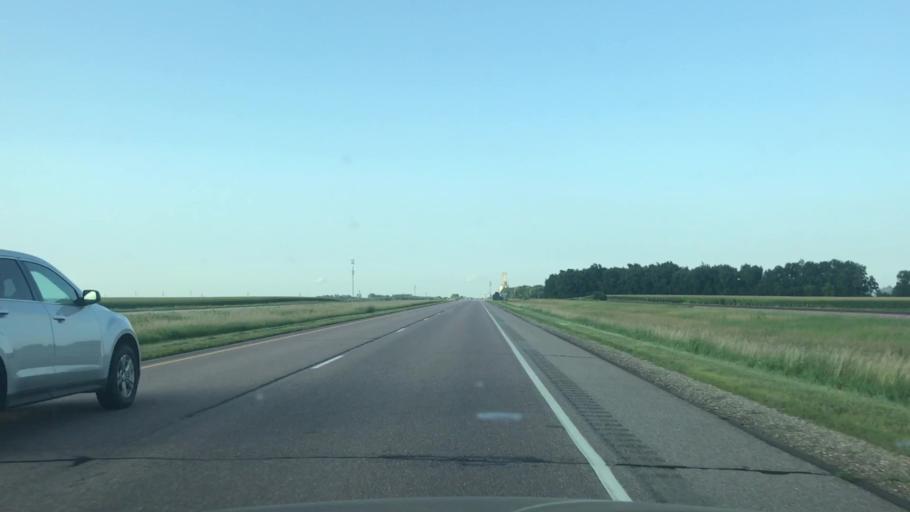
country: US
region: Minnesota
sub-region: Jackson County
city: Lakefield
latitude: 43.7561
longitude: -95.3828
